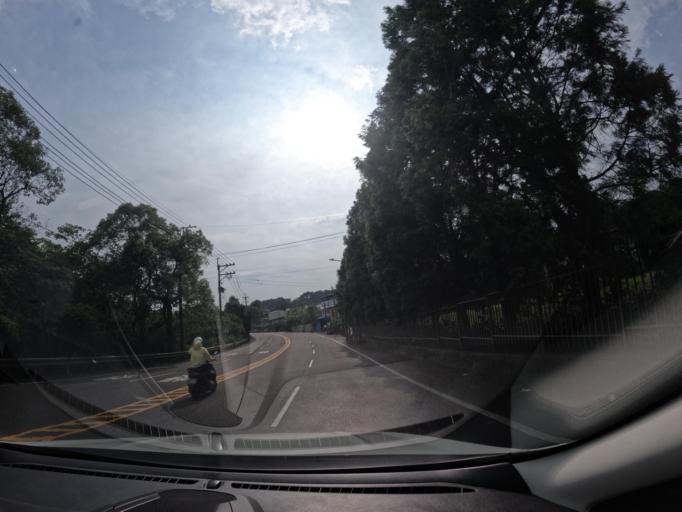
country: TW
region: Taiwan
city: Daxi
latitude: 24.8959
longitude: 121.3224
